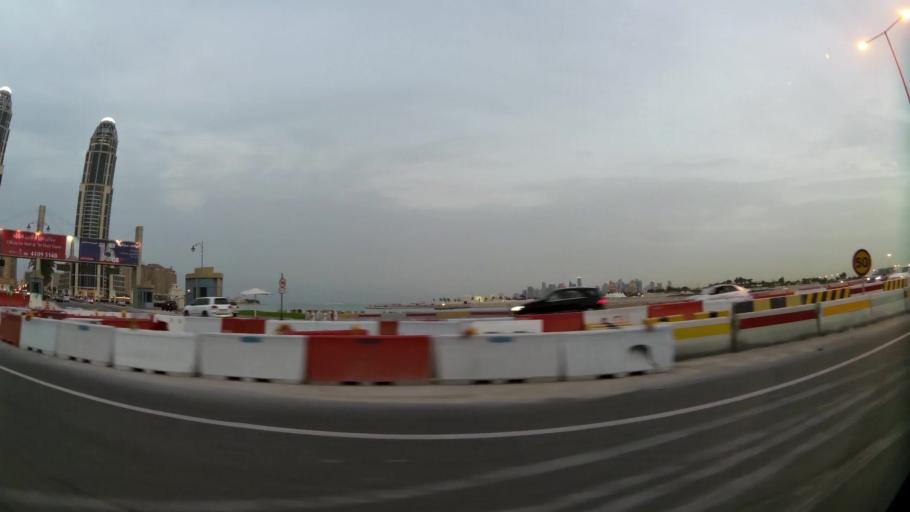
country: QA
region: Baladiyat ad Dawhah
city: Doha
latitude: 25.3732
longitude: 51.5282
